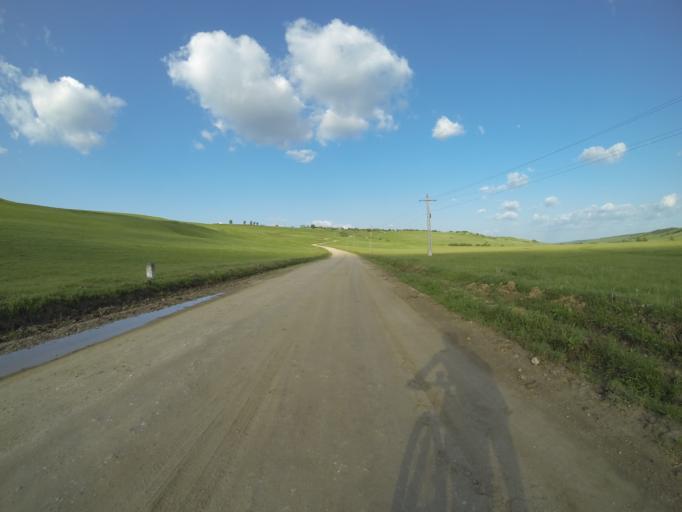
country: RO
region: Dolj
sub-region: Comuna Carpen
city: Carpen
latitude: 44.2920
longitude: 23.2813
